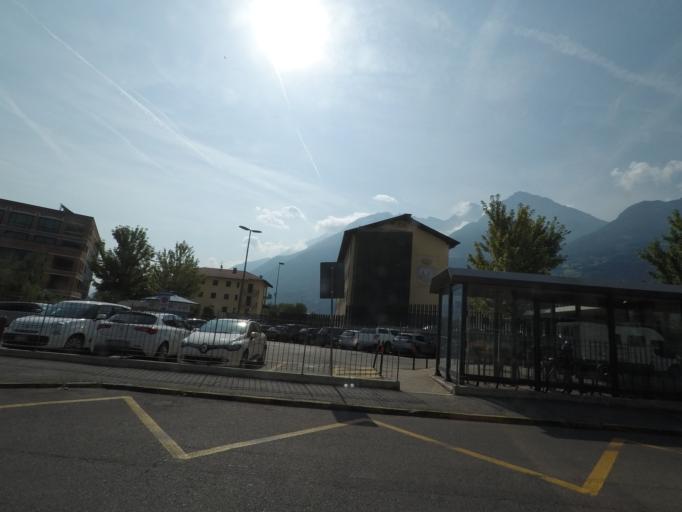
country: IT
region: Aosta Valley
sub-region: Valle d'Aosta
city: Aosta
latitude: 45.7388
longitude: 7.3358
